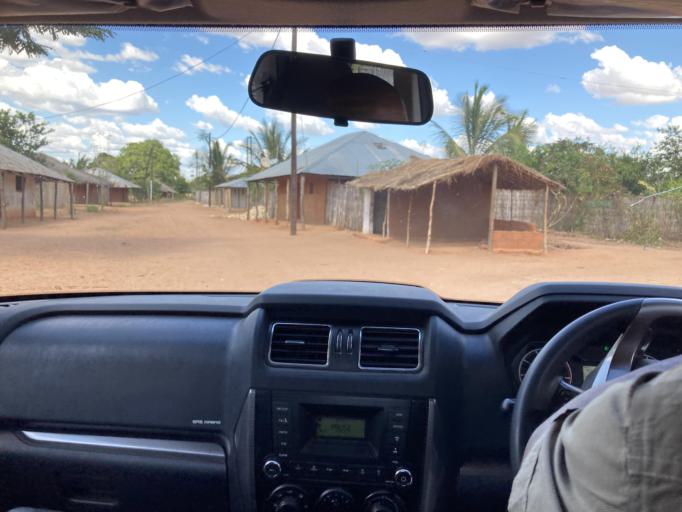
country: MZ
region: Cabo Delgado
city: Montepuez
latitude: -13.1460
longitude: 38.9851
